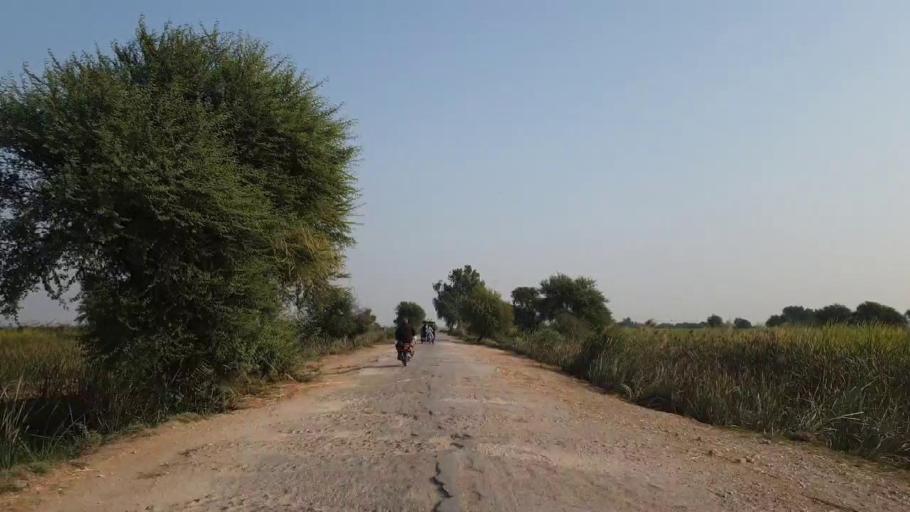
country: PK
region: Sindh
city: Bulri
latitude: 24.9760
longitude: 68.3982
